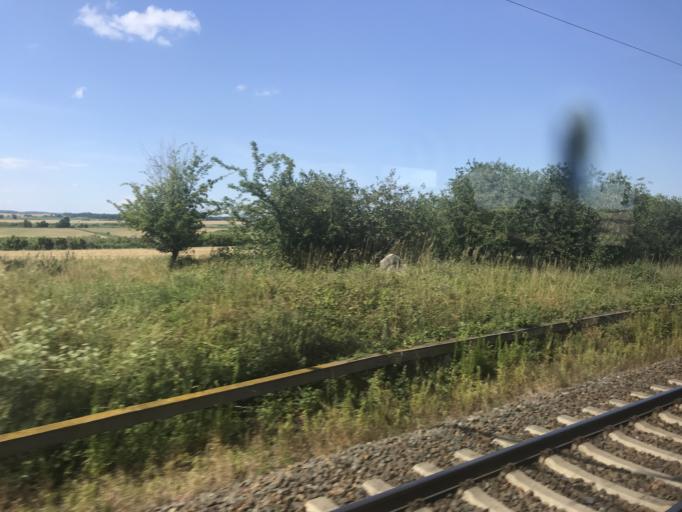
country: DE
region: Brandenburg
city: Angermunde
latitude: 53.0901
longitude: 14.0070
